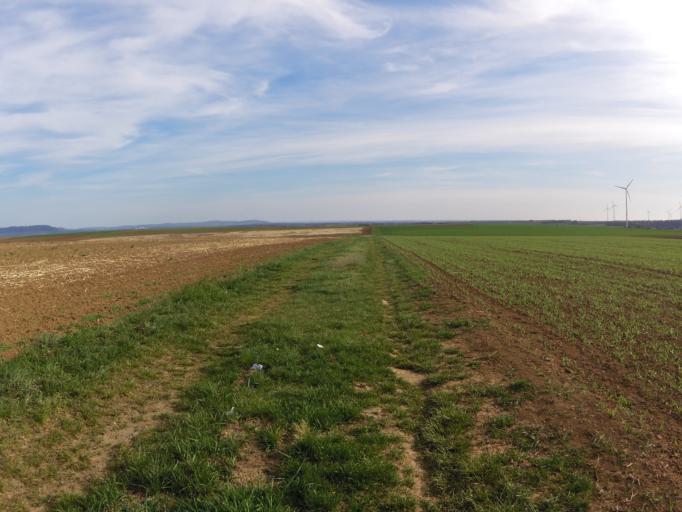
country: DE
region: Bavaria
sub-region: Regierungsbezirk Unterfranken
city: Mainstockheim
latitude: 49.7960
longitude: 10.1319
